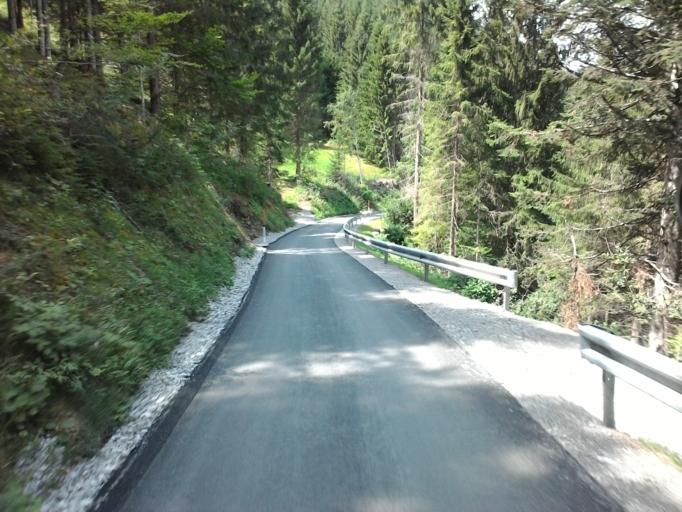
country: AT
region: Tyrol
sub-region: Politischer Bezirk Lienz
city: Untertilliach
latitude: 46.6992
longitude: 12.7717
